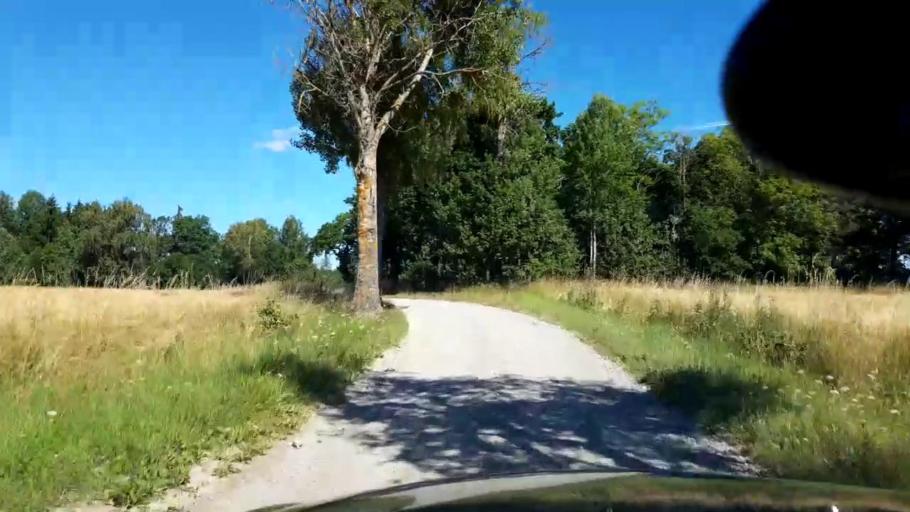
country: SE
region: Stockholm
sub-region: Sigtuna Kommun
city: Sigtuna
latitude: 59.6134
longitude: 17.6375
